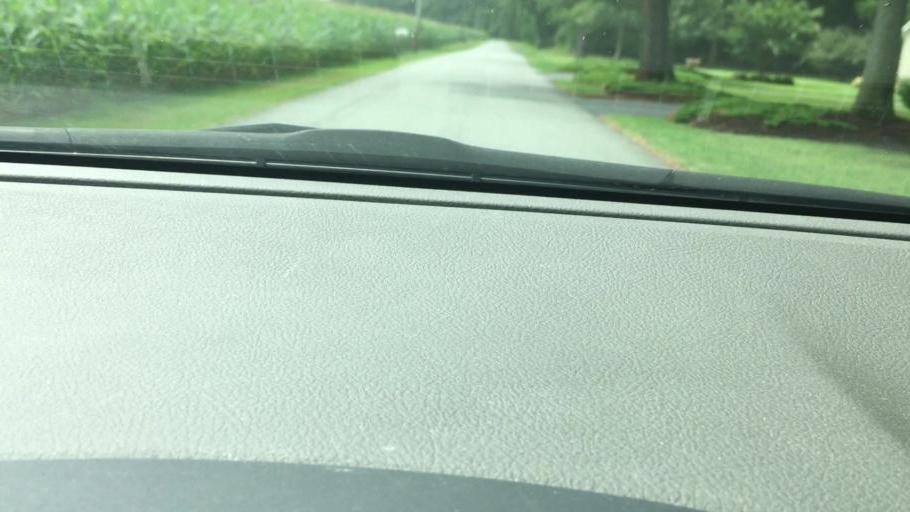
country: US
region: Maryland
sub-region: Worcester County
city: Pocomoke City
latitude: 38.0651
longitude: -75.5048
